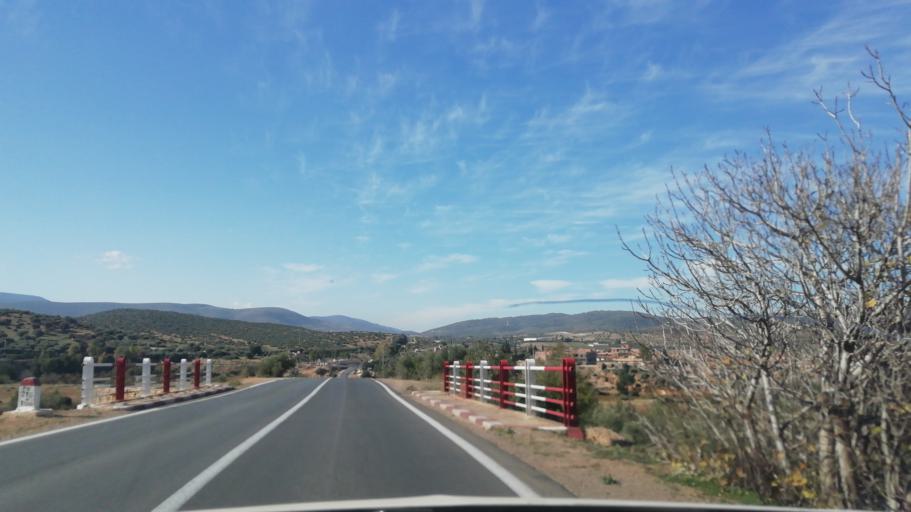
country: DZ
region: Tlemcen
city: Ouled Mimoun
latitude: 34.8688
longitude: -1.1317
